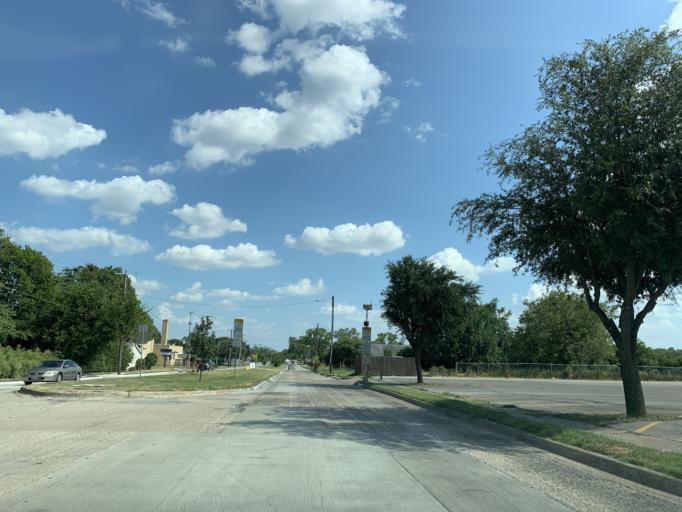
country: US
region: Texas
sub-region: Dallas County
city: Hutchins
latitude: 32.6989
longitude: -96.7751
